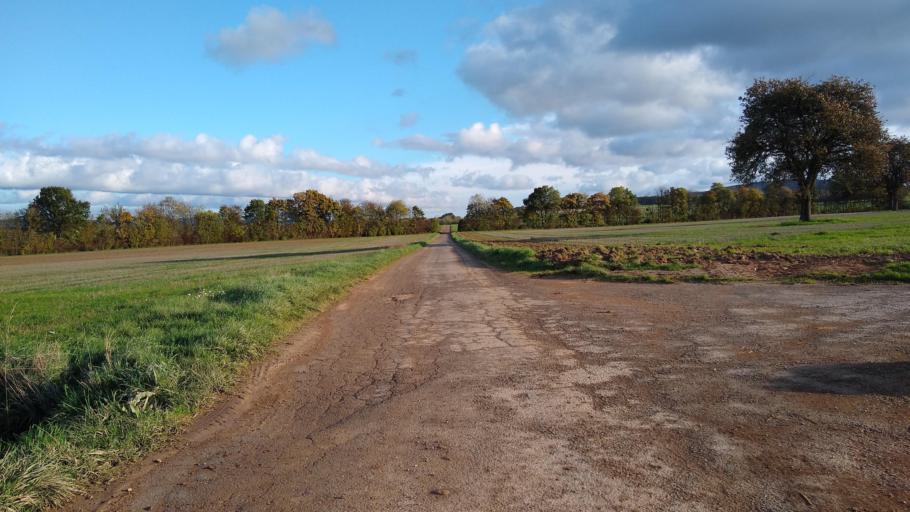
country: DE
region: Rheinland-Pfalz
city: Bekond
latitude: 49.8578
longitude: 6.8147
